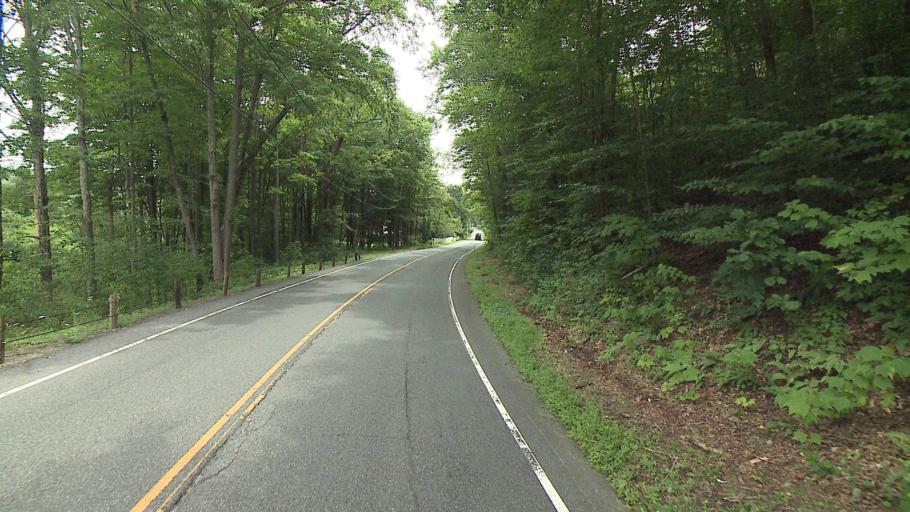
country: US
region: Connecticut
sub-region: Litchfield County
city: Bethlehem Village
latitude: 41.5985
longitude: -73.2702
